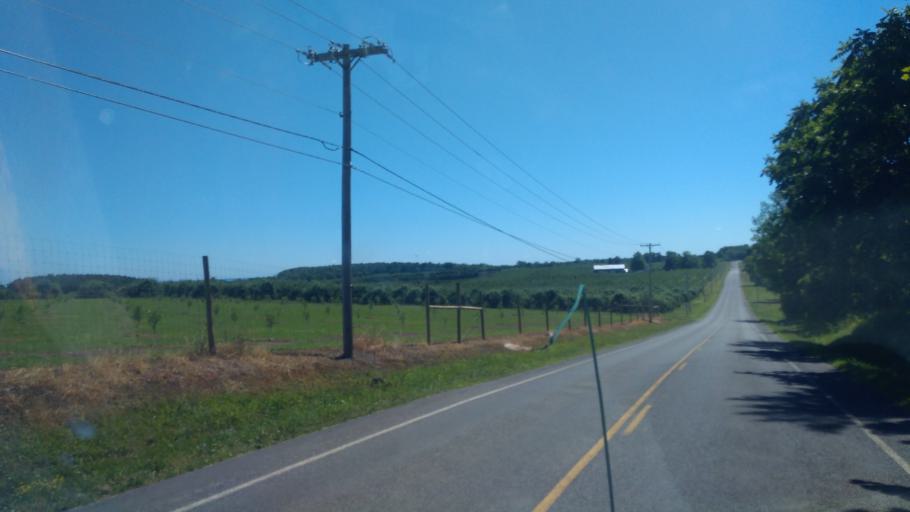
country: US
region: New York
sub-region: Wayne County
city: Sodus
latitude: 43.2721
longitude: -77.0957
